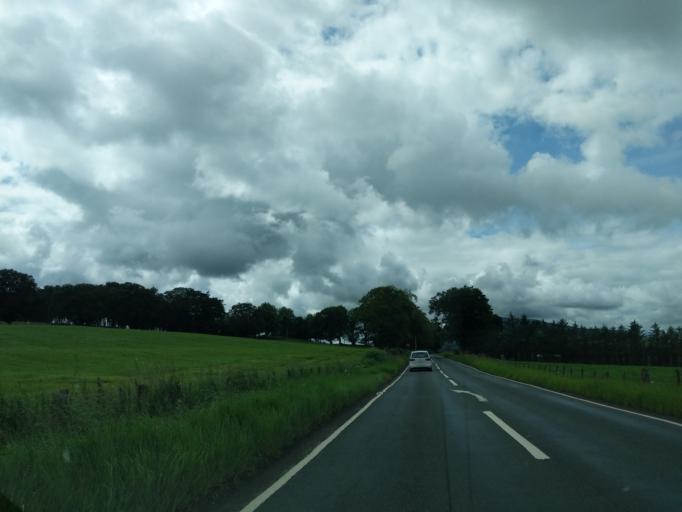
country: GB
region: Scotland
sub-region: South Lanarkshire
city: Biggar
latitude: 55.6120
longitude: -3.5482
